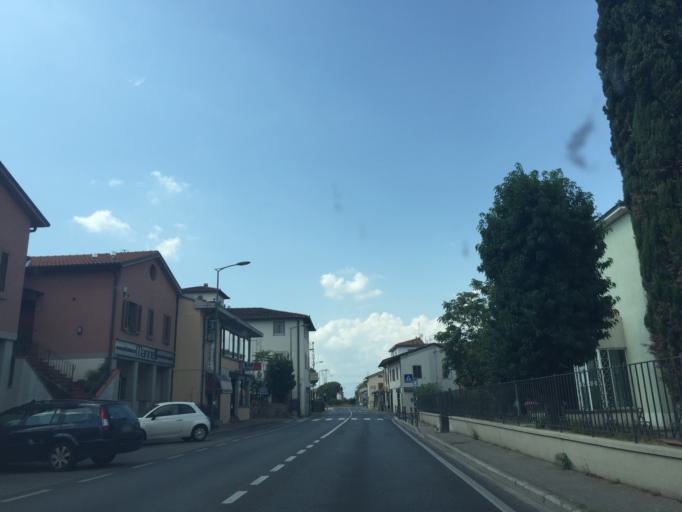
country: IT
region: Tuscany
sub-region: Provincia di Prato
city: Poggetto
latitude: 43.8275
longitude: 11.0402
